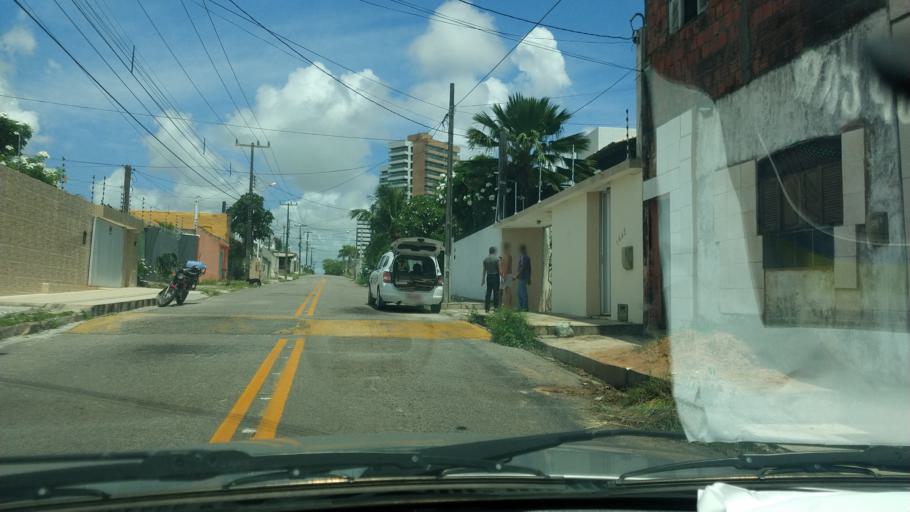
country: BR
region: Rio Grande do Norte
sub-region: Natal
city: Natal
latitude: -5.8660
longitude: -35.1983
